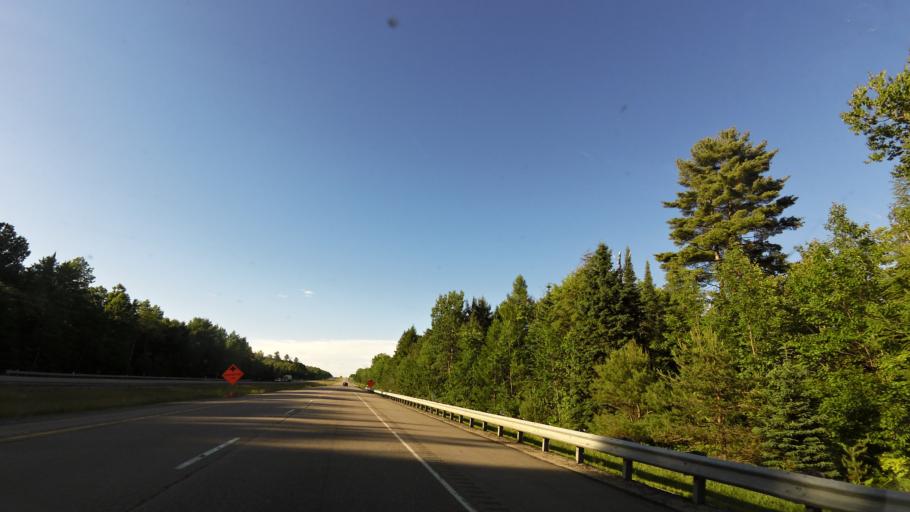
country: CA
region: Ontario
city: Orillia
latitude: 44.6383
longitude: -79.6538
